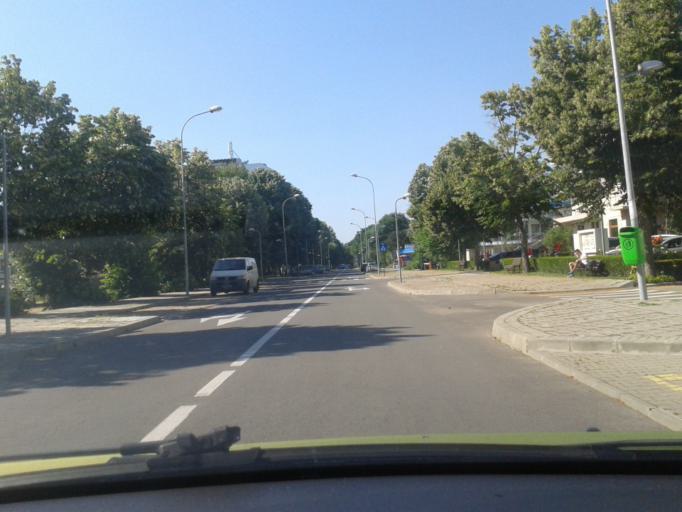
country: RO
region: Constanta
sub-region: Comuna Douazeci si Trei August
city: Douazeci si Trei August
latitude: 43.8802
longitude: 28.6031
